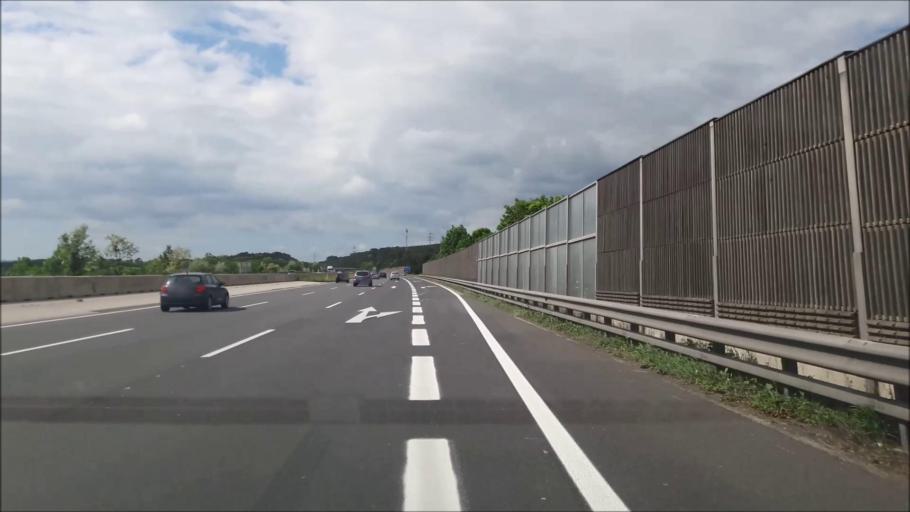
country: AT
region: Lower Austria
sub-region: Politischer Bezirk Wiener Neustadt
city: Theresienfeld
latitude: 47.8619
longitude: 16.1872
